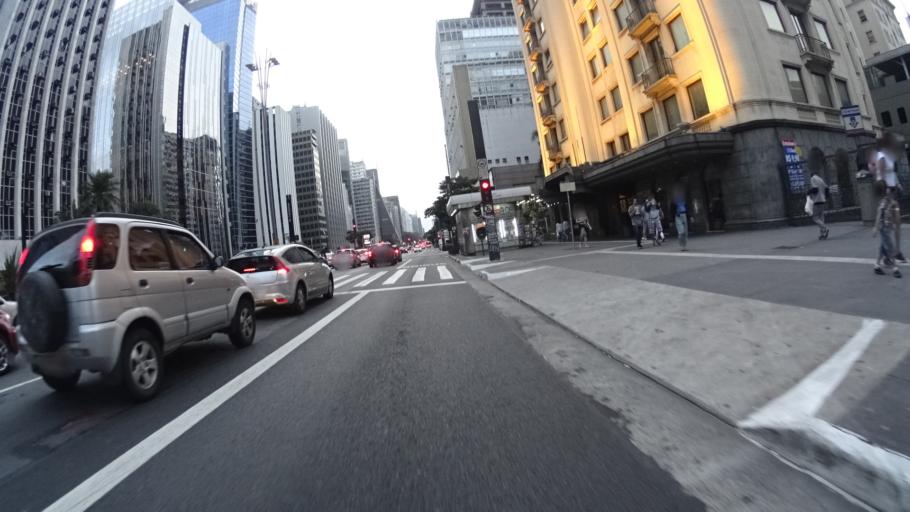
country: BR
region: Sao Paulo
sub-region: Sao Paulo
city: Sao Paulo
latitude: -23.5665
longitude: -46.6503
